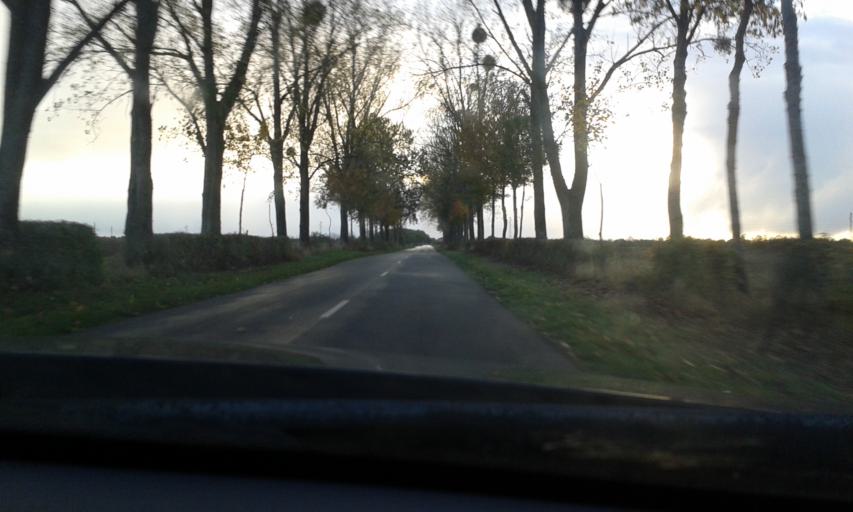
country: FR
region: Centre
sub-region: Departement du Loiret
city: Chevilly
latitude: 48.0185
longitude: 1.8534
